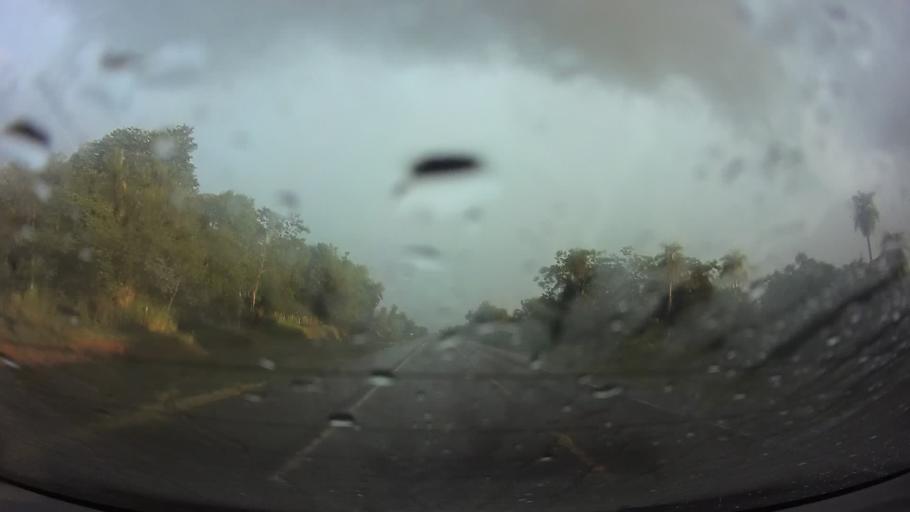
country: PY
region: Paraguari
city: Paraguari
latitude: -25.6176
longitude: -57.1754
